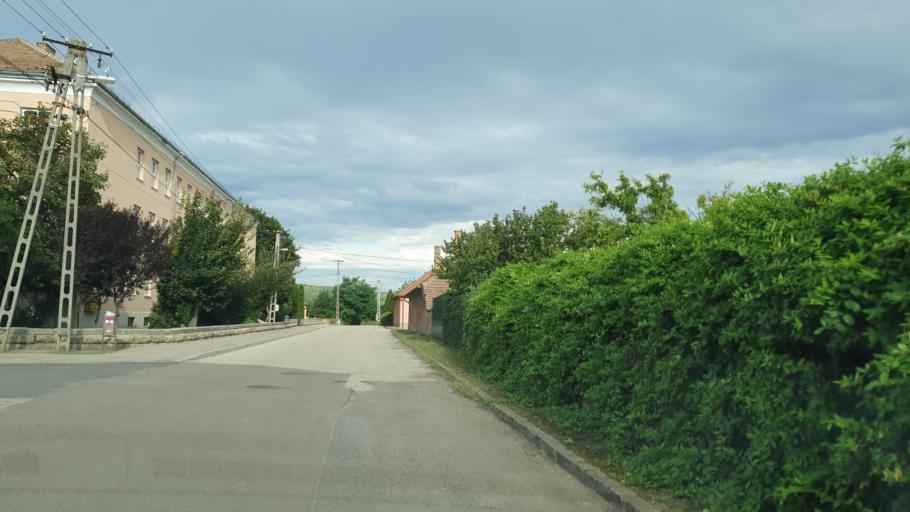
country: HU
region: Heves
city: Zagyvaszanto
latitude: 47.7569
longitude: 19.6795
